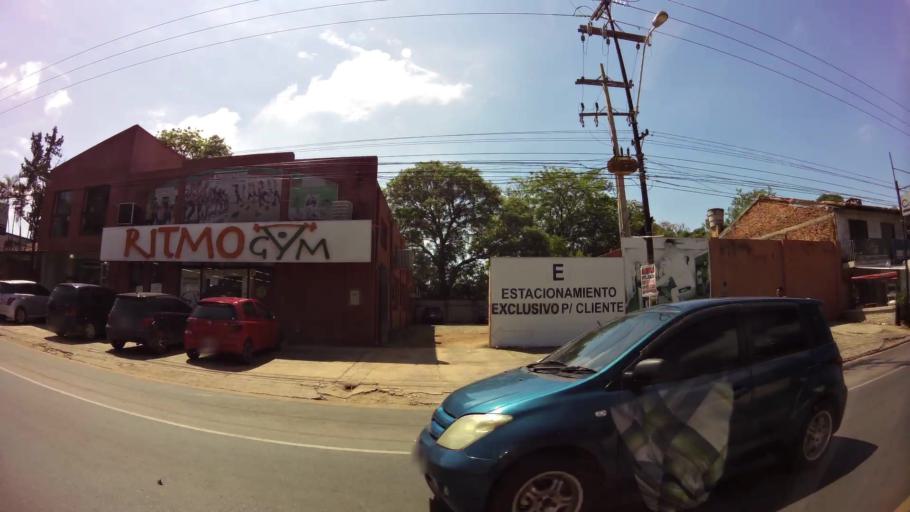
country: PY
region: Central
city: San Lorenzo
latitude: -25.3314
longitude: -57.5102
